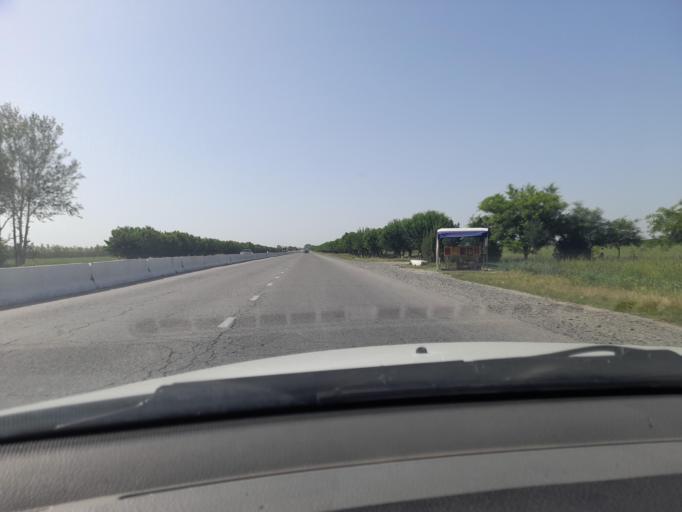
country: UZ
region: Samarqand
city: Daxbet
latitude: 39.8213
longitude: 66.8446
